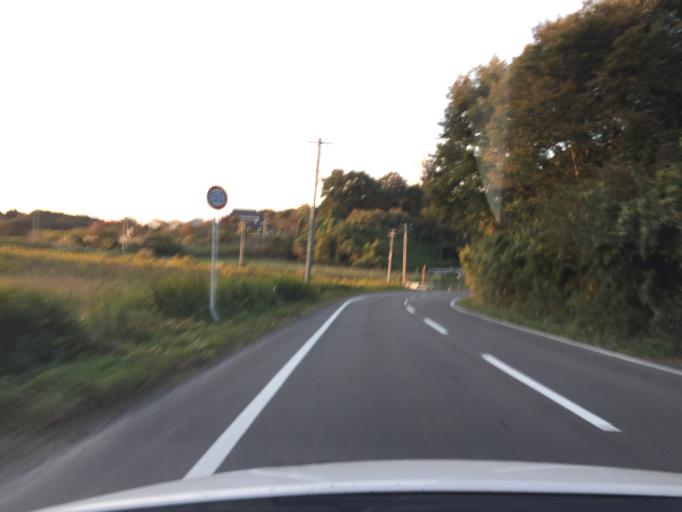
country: JP
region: Fukushima
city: Sukagawa
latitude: 37.3342
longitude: 140.4409
